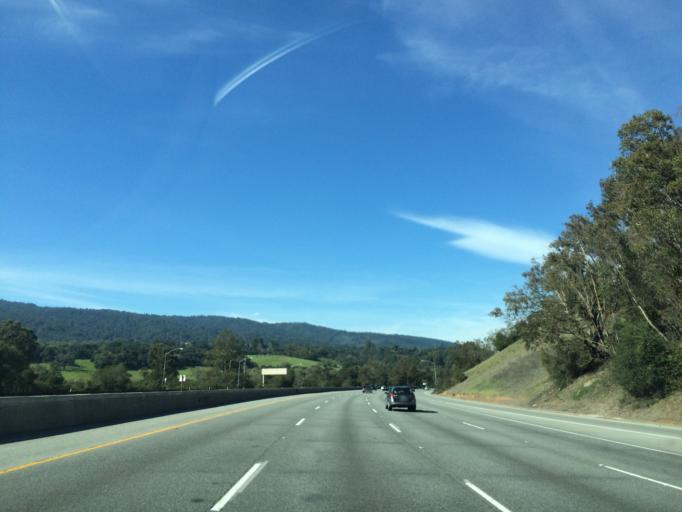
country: US
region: California
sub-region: San Mateo County
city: Woodside
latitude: 37.4440
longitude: -122.2659
